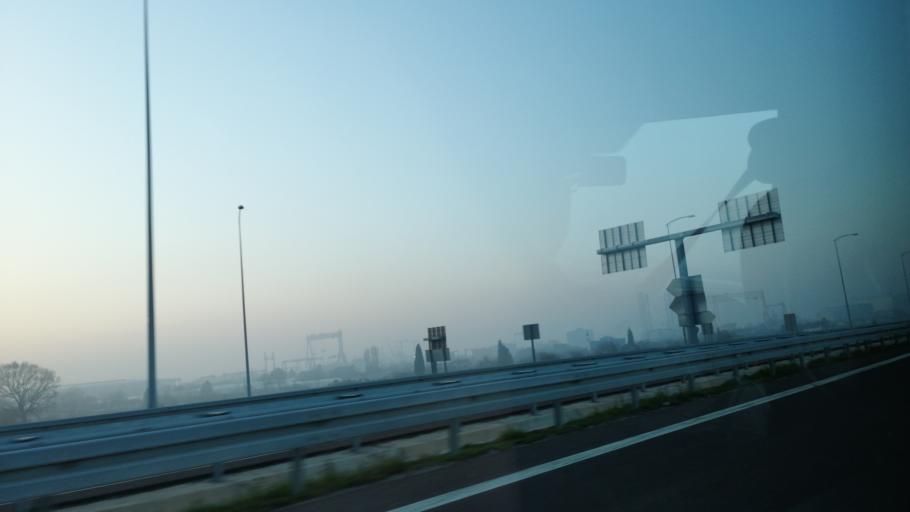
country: TR
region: Yalova
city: Altinova
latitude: 40.6917
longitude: 29.4704
